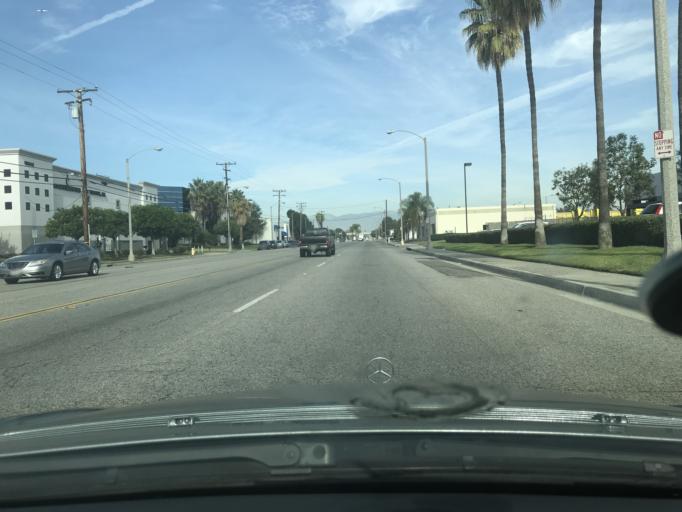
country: US
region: California
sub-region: Los Angeles County
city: Santa Fe Springs
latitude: 33.9364
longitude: -118.0726
